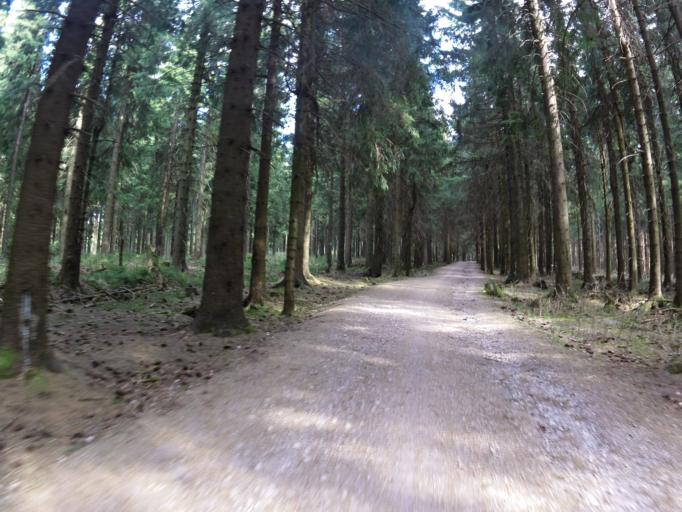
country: DE
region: Thuringia
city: Oberhof
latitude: 50.7045
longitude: 10.7001
